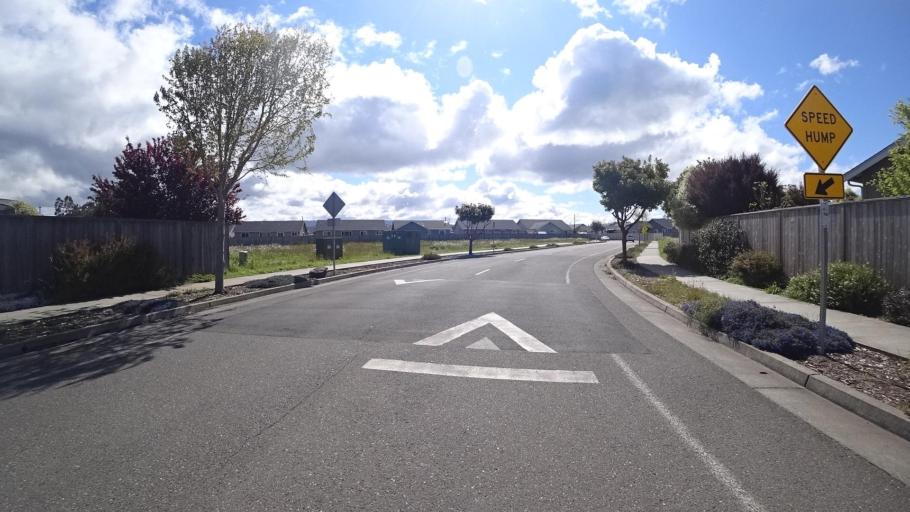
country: US
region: California
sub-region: Humboldt County
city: McKinleyville
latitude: 40.9395
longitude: -124.1090
